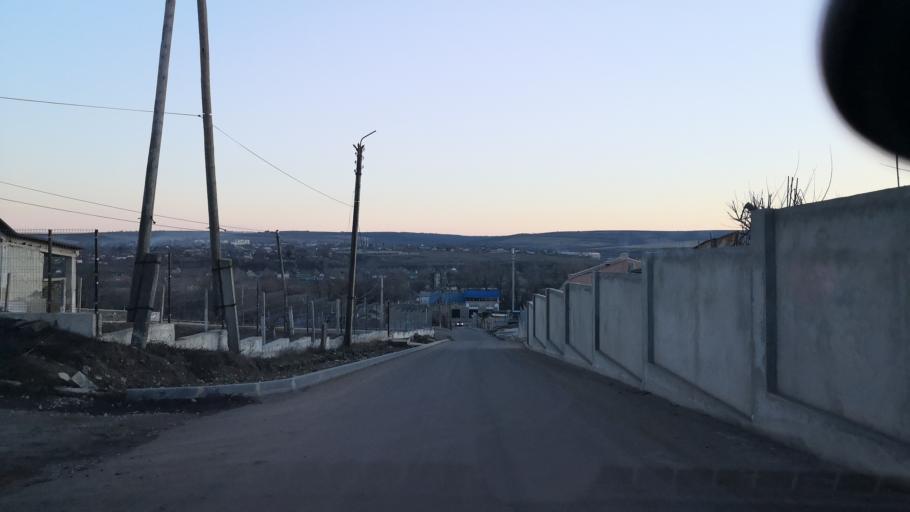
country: MD
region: Anenii Noi
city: Anenii Noi
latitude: 46.8929
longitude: 29.2928
